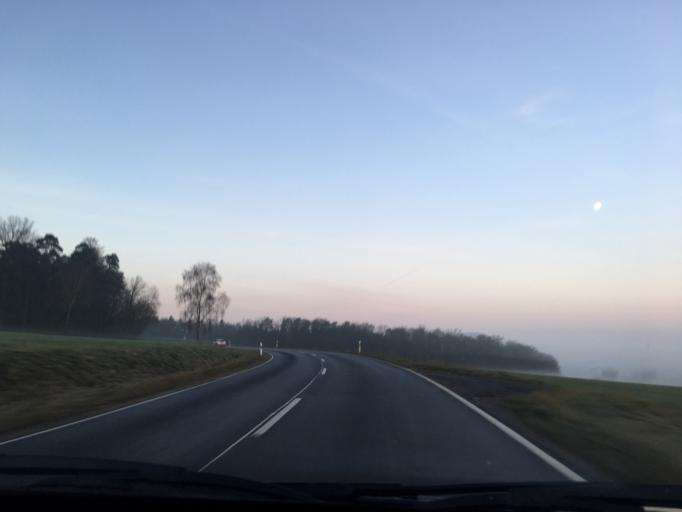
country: DE
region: Hesse
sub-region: Regierungsbezirk Kassel
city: Dipperz
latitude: 50.5751
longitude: 9.7799
